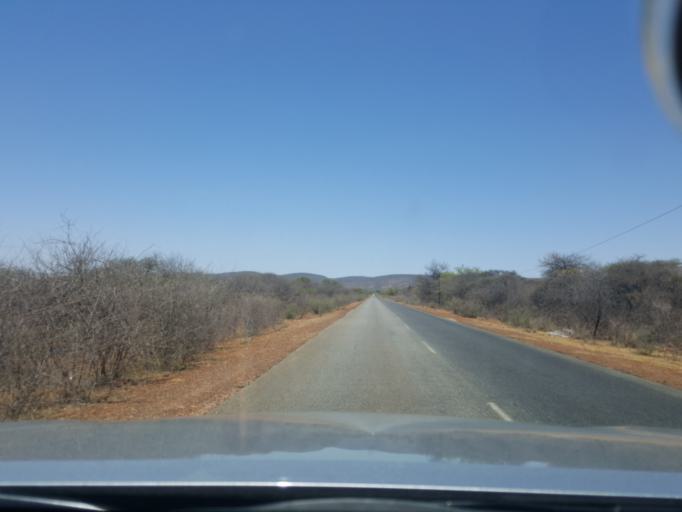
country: BW
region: South East
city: Lobatse
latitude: -25.2456
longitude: 25.9325
